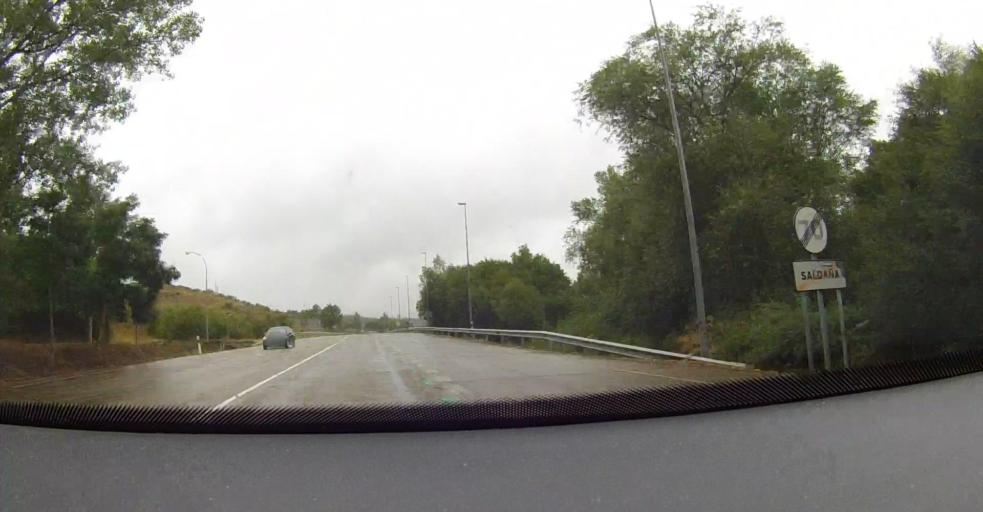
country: ES
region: Castille and Leon
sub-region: Provincia de Palencia
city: Saldana
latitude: 42.5293
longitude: -4.7339
